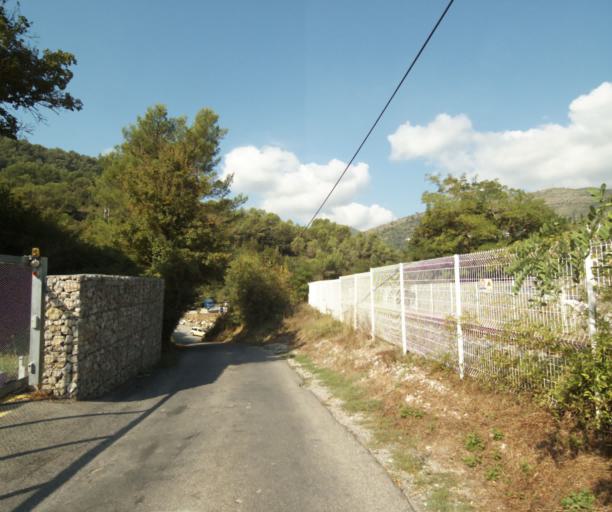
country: FR
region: Provence-Alpes-Cote d'Azur
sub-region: Departement des Alpes-Maritimes
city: Drap
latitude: 43.7638
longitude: 7.3375
